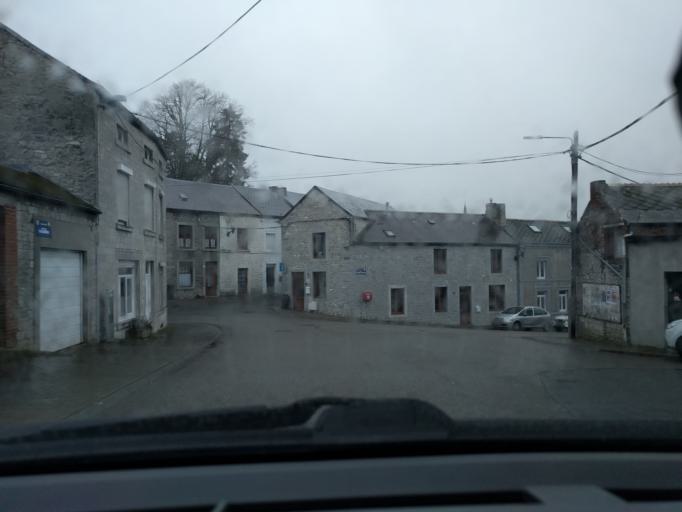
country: BE
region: Wallonia
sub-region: Province de Namur
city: Couvin
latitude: 50.0507
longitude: 4.4998
